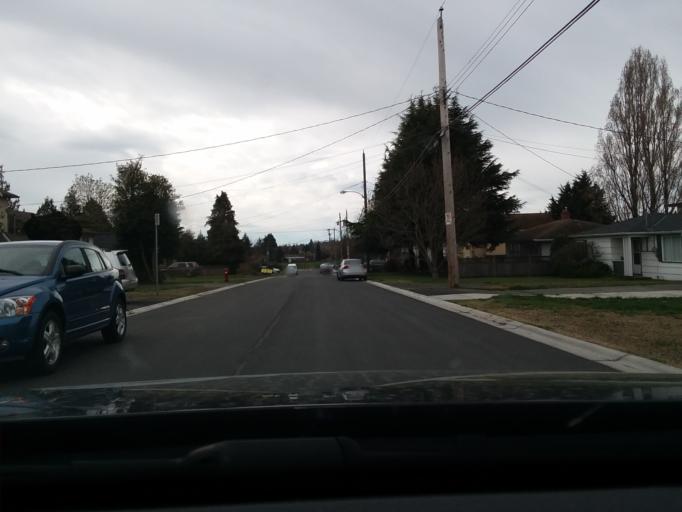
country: CA
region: British Columbia
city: Oak Bay
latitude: 48.4476
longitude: -123.3319
